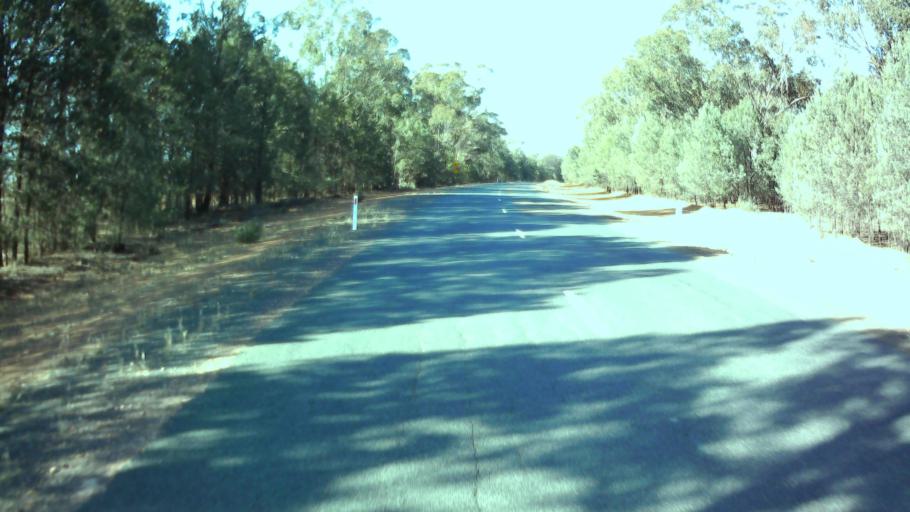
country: AU
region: New South Wales
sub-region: Weddin
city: Grenfell
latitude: -34.0301
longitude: 148.0938
